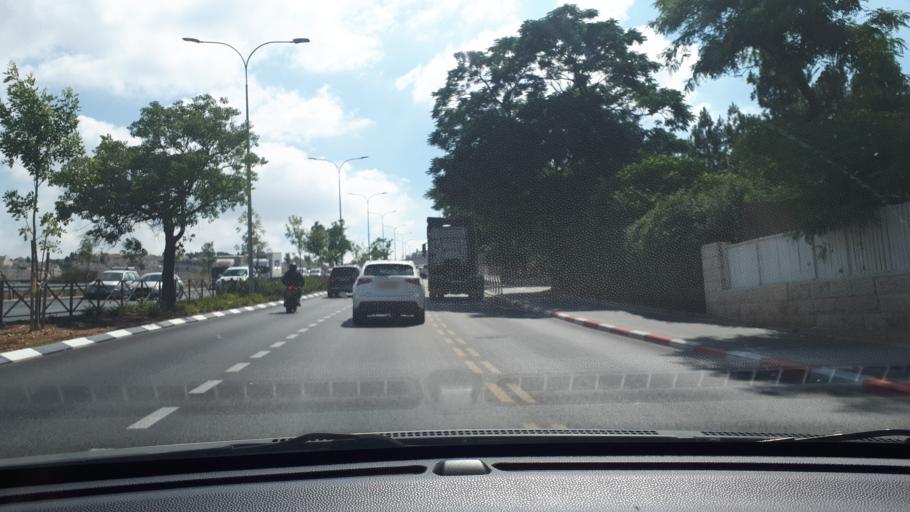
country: PS
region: West Bank
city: Hizma
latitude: 31.8266
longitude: 35.2443
